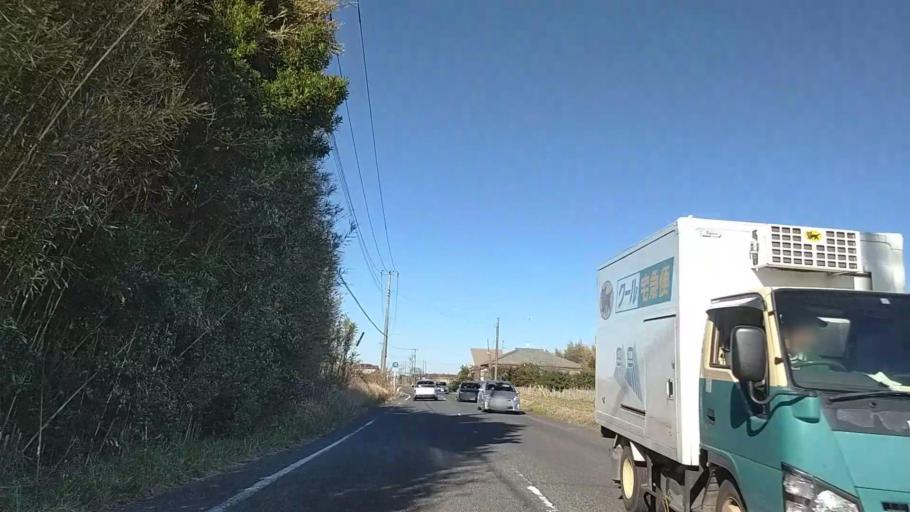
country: JP
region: Chiba
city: Mobara
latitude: 35.4057
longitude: 140.3878
